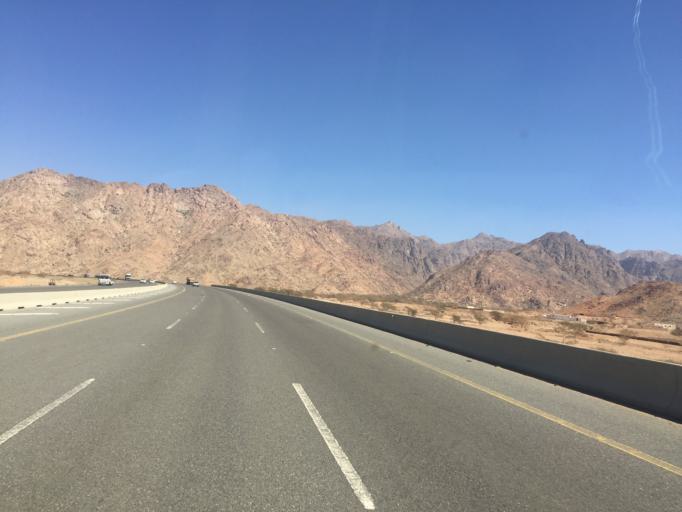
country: SA
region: Al Madinah al Munawwarah
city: Badr Hunayn
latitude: 24.0649
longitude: 39.2036
